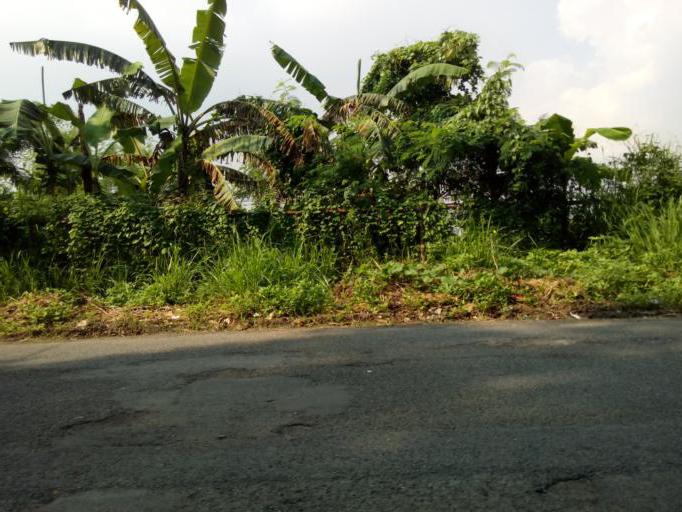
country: PH
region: Metro Manila
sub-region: Quezon City
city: Quezon City
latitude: 14.6459
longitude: 121.0683
